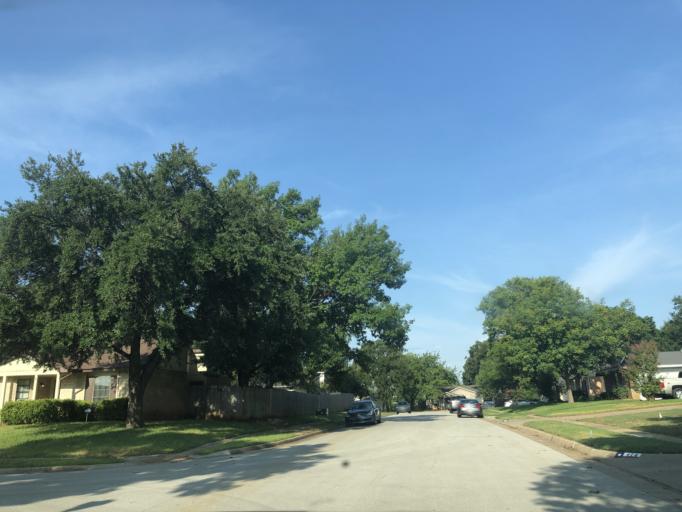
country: US
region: Texas
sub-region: Tarrant County
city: Euless
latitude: 32.8753
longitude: -97.0893
